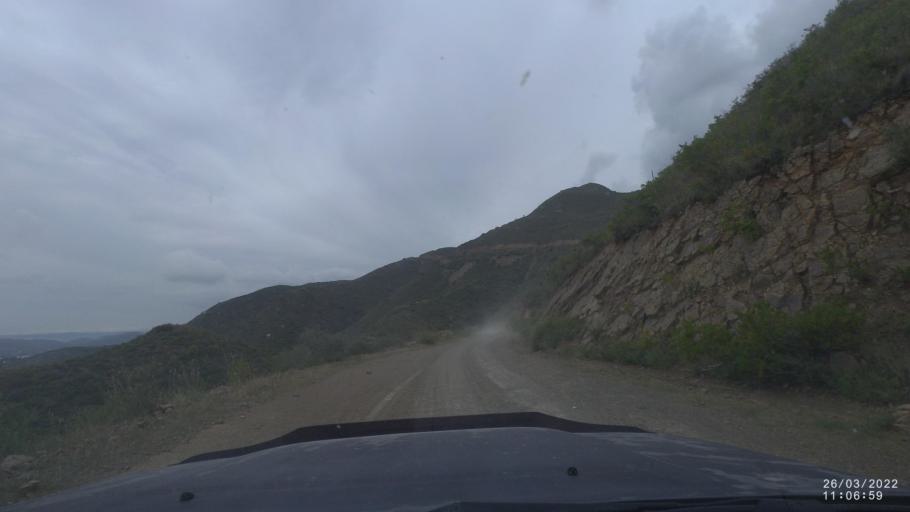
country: BO
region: Cochabamba
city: Tarata
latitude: -17.5351
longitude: -66.0175
